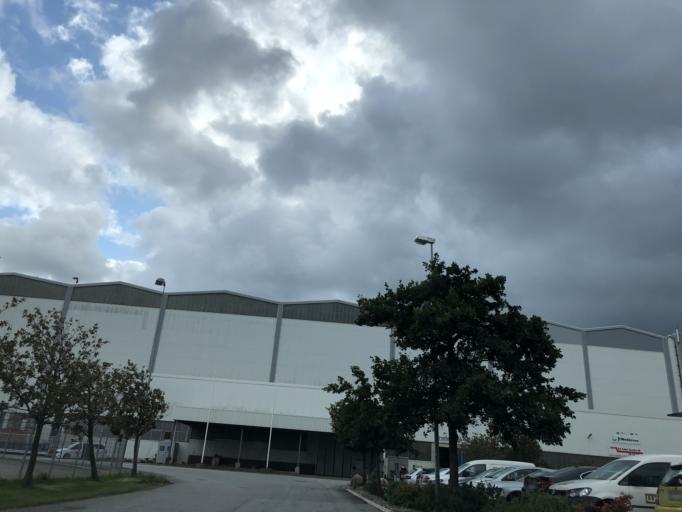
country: SE
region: Vaestra Goetaland
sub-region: Goteborg
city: Torslanda
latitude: 57.6984
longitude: 11.8210
